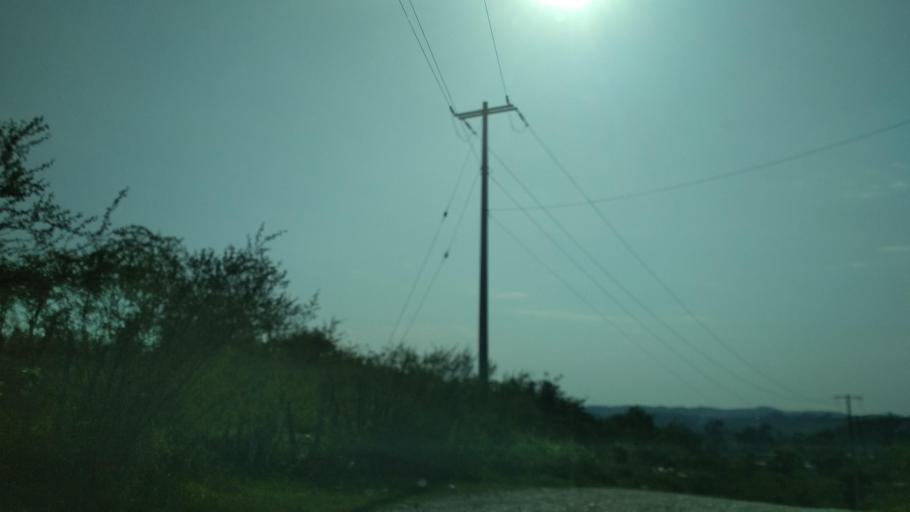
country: MM
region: Shan
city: Taunggyi
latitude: 20.4006
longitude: 97.3302
